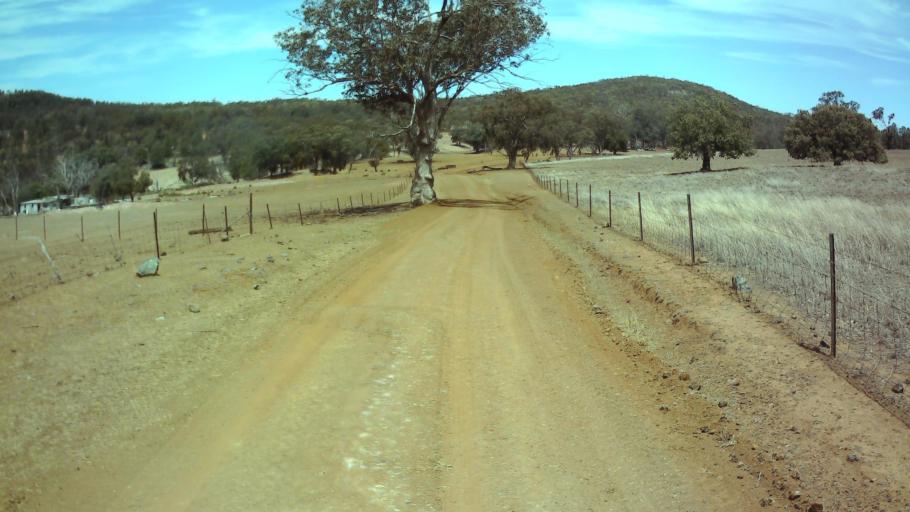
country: AU
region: New South Wales
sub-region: Weddin
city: Grenfell
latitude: -33.7895
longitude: 148.1569
